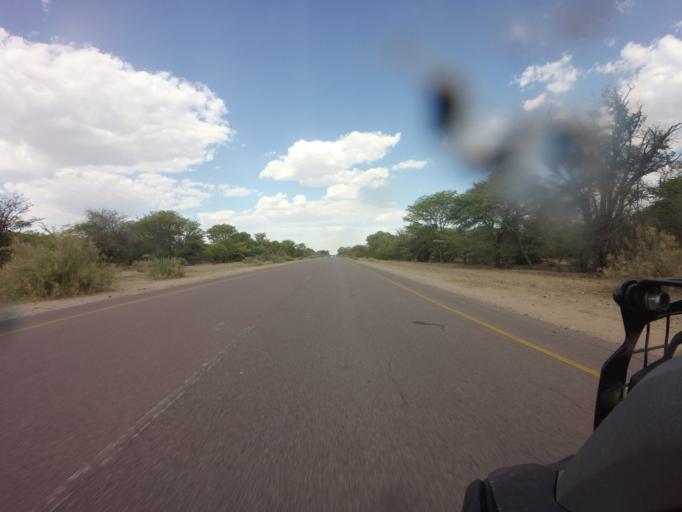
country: AO
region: Cunene
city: Ondjiva
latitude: -16.7412
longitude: 15.1195
